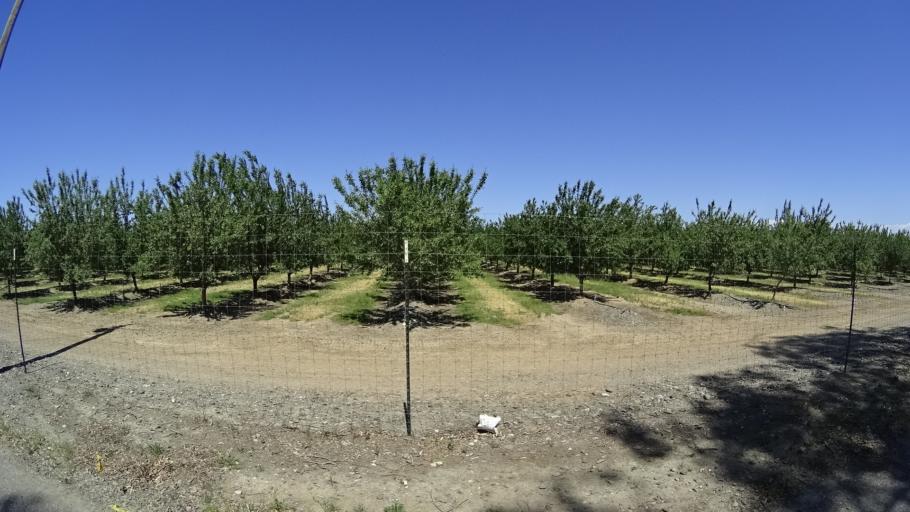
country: US
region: California
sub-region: Glenn County
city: Orland
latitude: 39.7914
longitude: -122.2339
